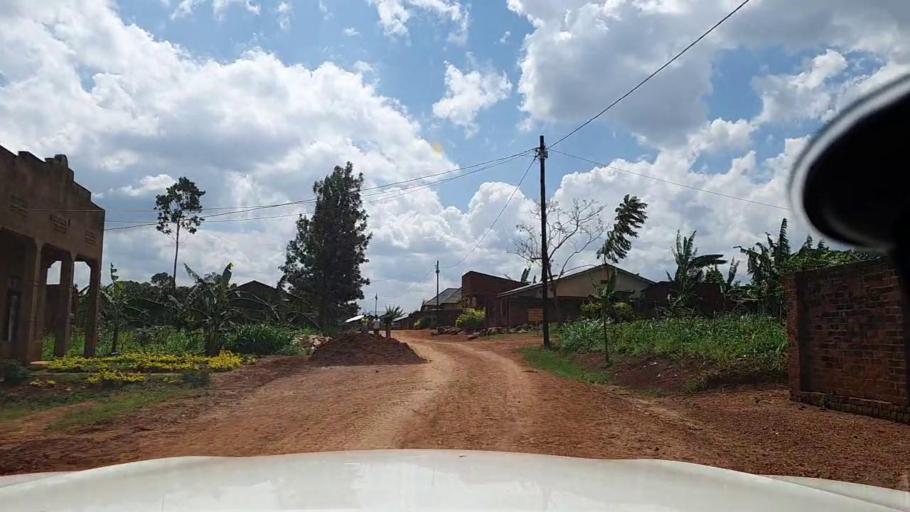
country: RW
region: Kigali
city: Kigali
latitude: -1.8343
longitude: 29.8353
